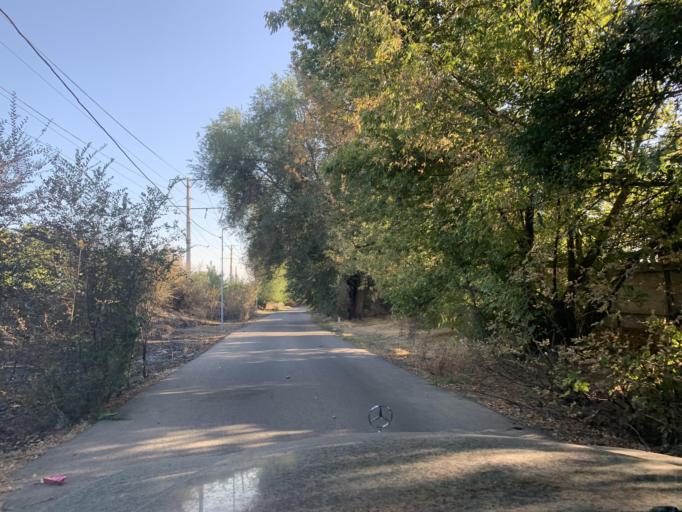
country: KZ
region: Almaty Oblysy
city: Energeticheskiy
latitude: 43.3915
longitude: 77.0000
